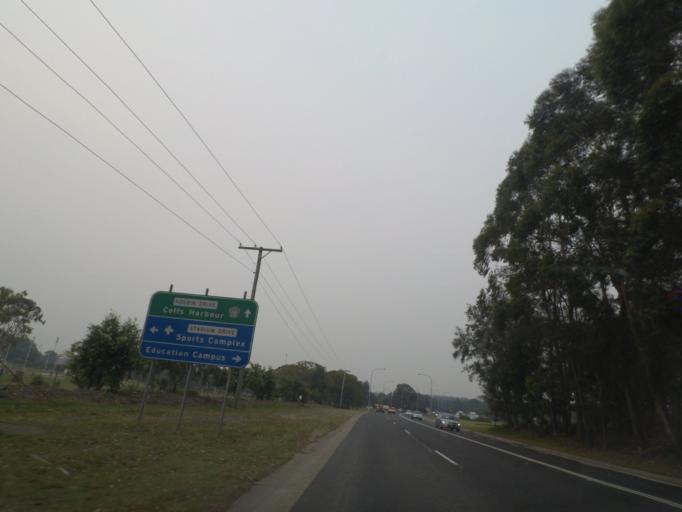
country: AU
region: New South Wales
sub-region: Coffs Harbour
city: Toormina
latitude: -30.3276
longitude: 153.0982
